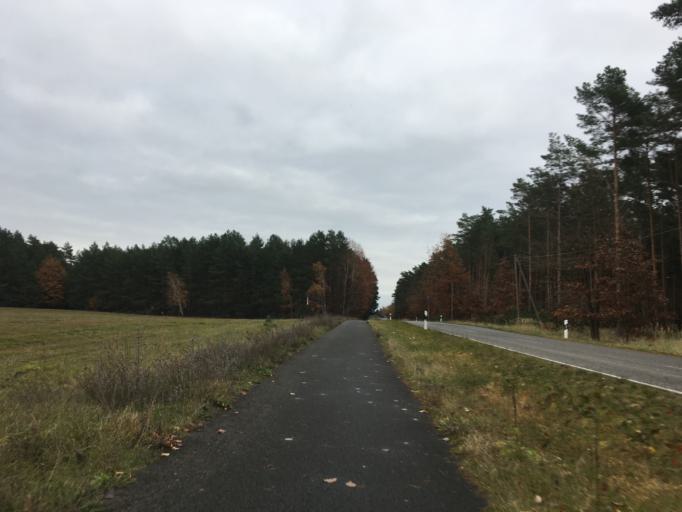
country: DE
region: Brandenburg
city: Mixdorf
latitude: 52.1865
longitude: 14.4512
